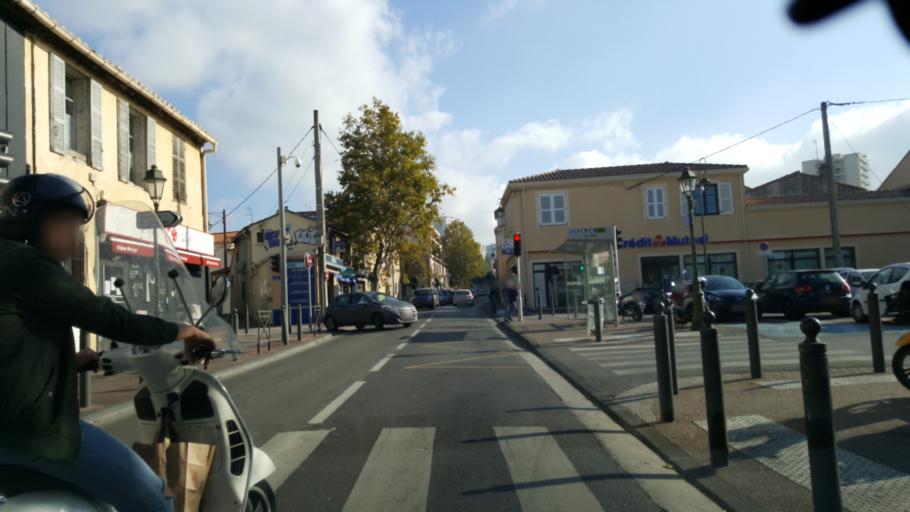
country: FR
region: Provence-Alpes-Cote d'Azur
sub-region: Departement des Bouches-du-Rhone
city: Marseille 09
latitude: 43.2589
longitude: 5.4171
